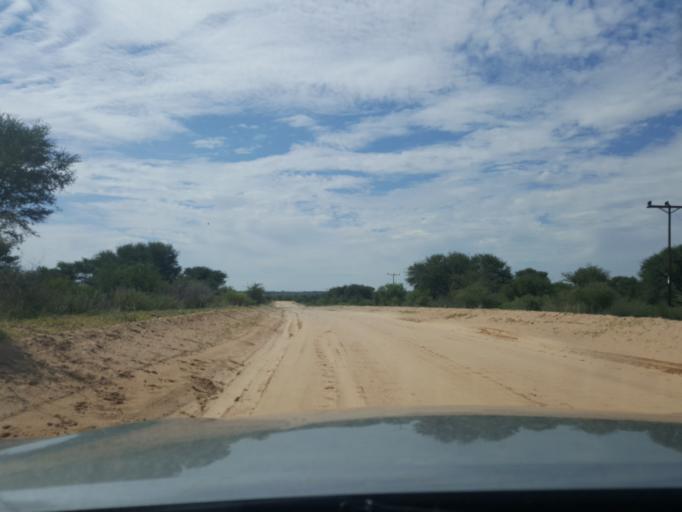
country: BW
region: Kweneng
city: Letlhakeng
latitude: -24.0618
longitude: 25.0311
